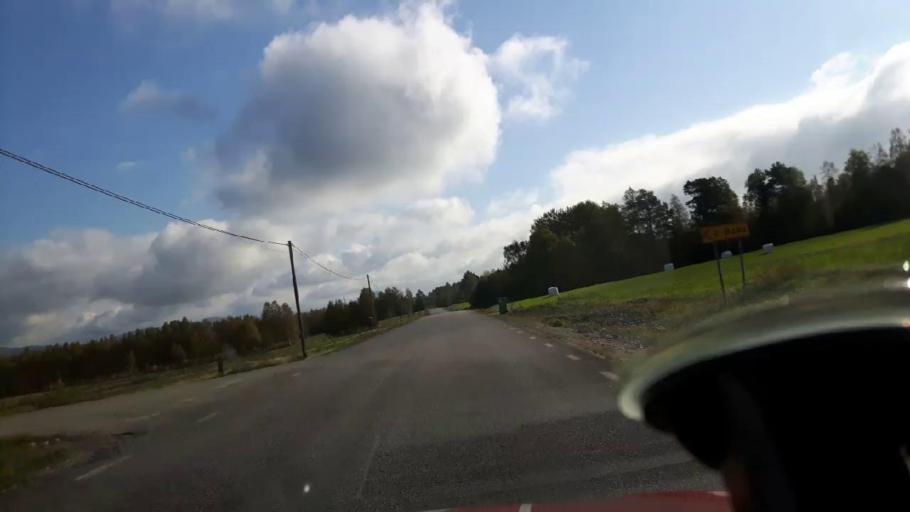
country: SE
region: Gaevleborg
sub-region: Ljusdals Kommun
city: Ljusdal
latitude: 61.7598
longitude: 16.0937
